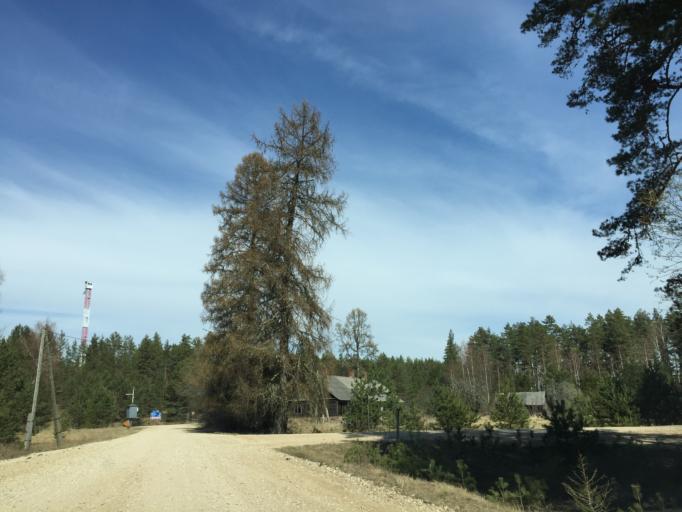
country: LV
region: Strenci
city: Seda
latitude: 57.6501
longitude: 25.8640
